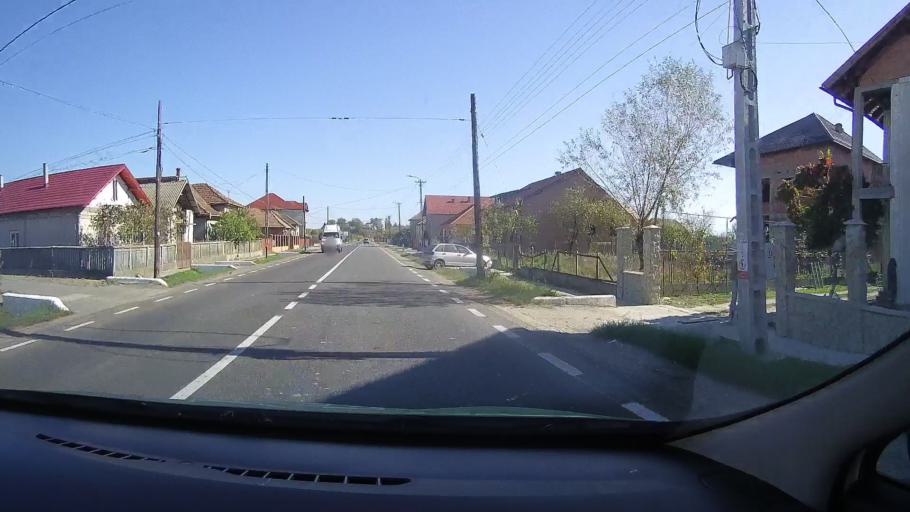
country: RO
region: Satu Mare
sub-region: Oras Ardud
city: Ardud
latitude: 47.6531
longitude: 22.8876
